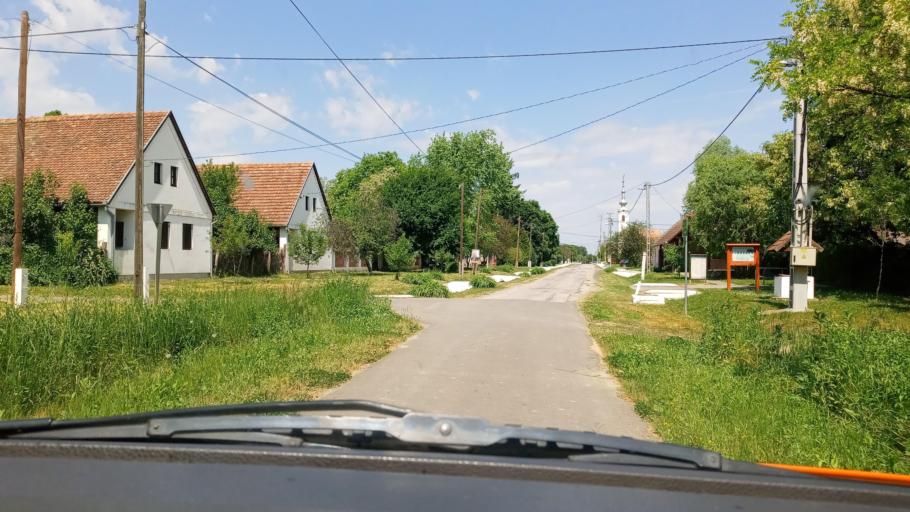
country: HR
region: Osjecko-Baranjska
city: Viljevo
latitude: 45.8090
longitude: 18.1164
